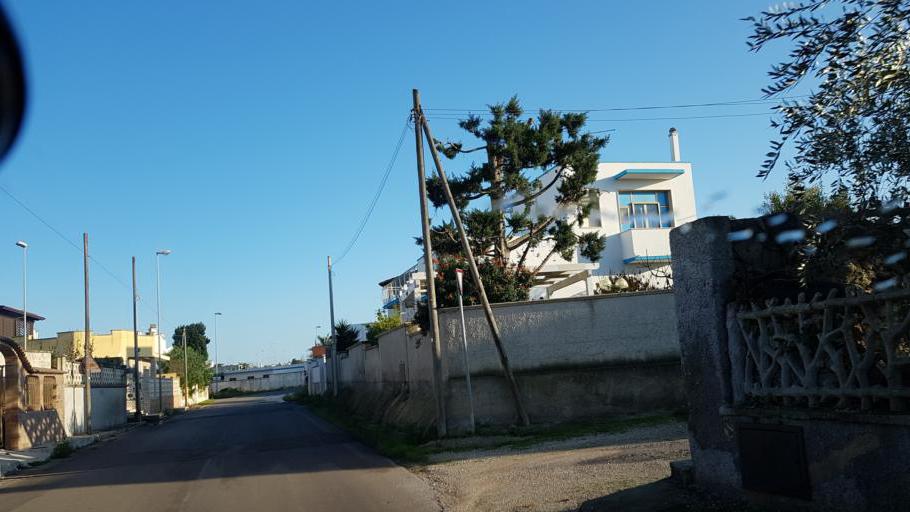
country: IT
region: Apulia
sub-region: Provincia di Brindisi
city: Torchiarolo
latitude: 40.5015
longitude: 18.1143
